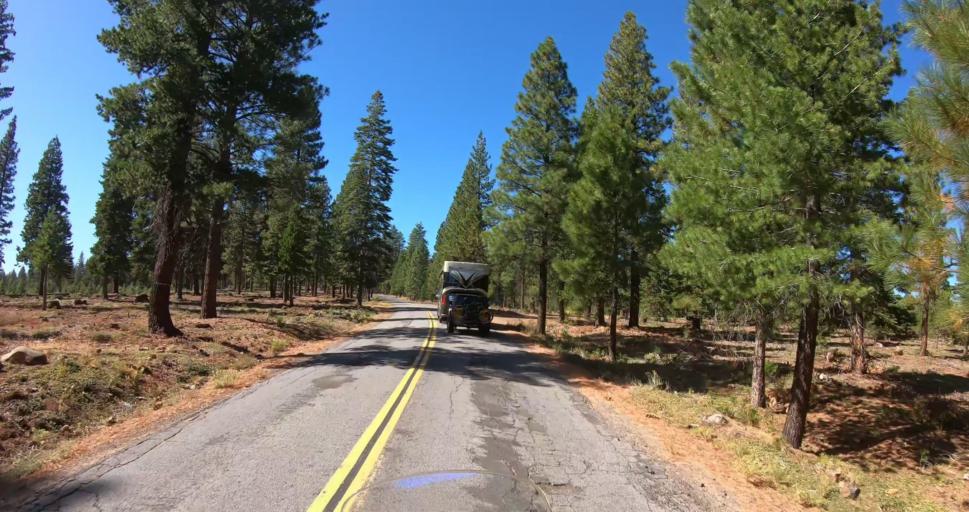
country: US
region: California
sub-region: Lassen County
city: Susanville
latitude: 40.4442
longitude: -120.7524
